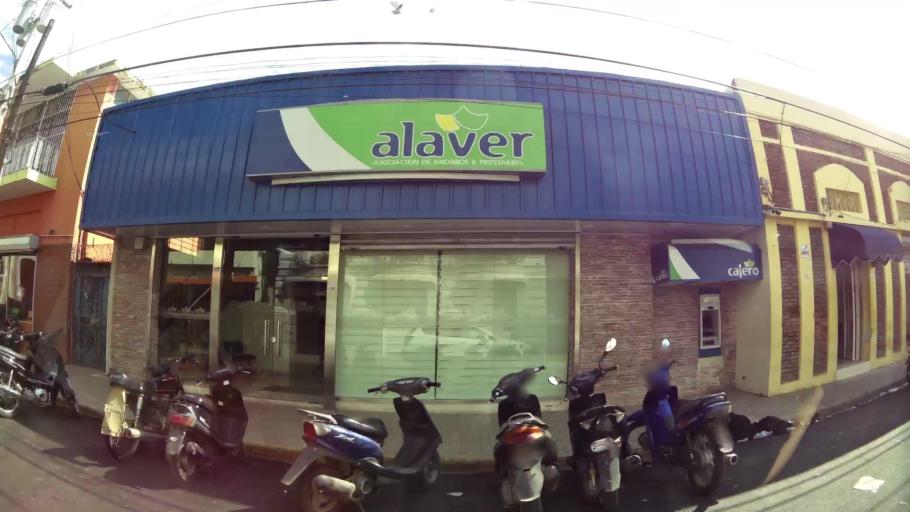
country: DO
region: La Vega
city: Concepcion de La Vega
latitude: 19.2241
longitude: -70.5313
